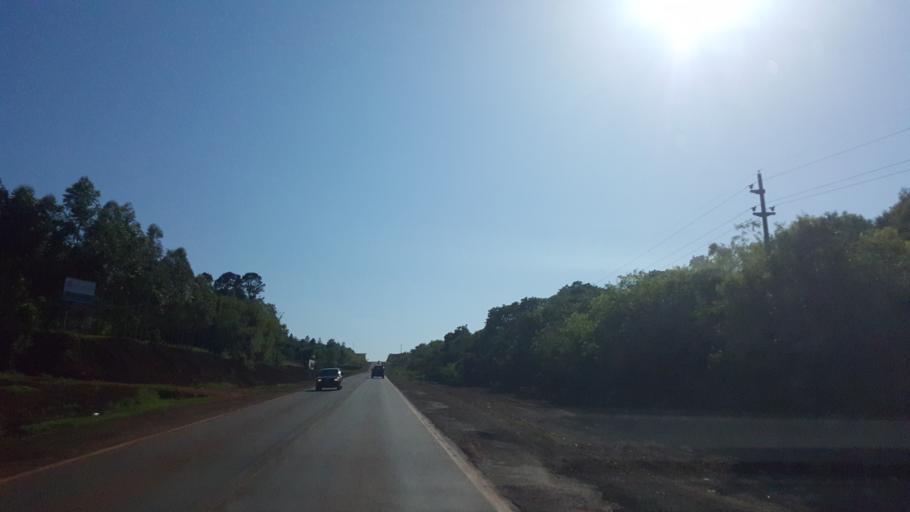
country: AR
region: Misiones
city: Santa Ana
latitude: -27.3743
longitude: -55.5715
